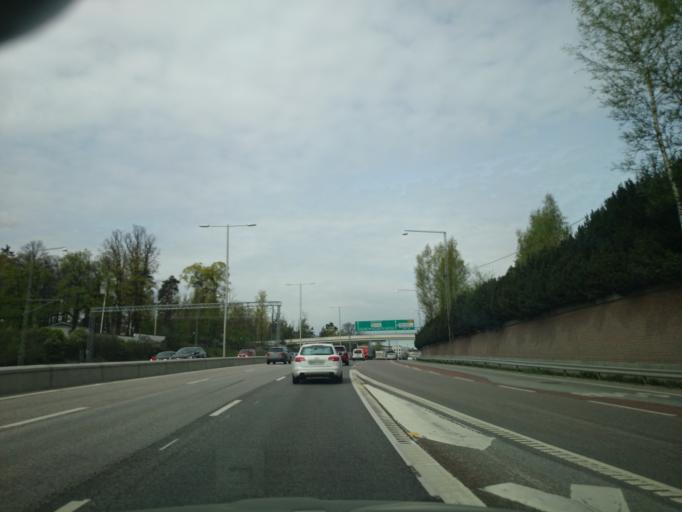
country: SE
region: Stockholm
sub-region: Norrtalje Kommun
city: Bergshamra
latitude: 59.3654
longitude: 18.0219
